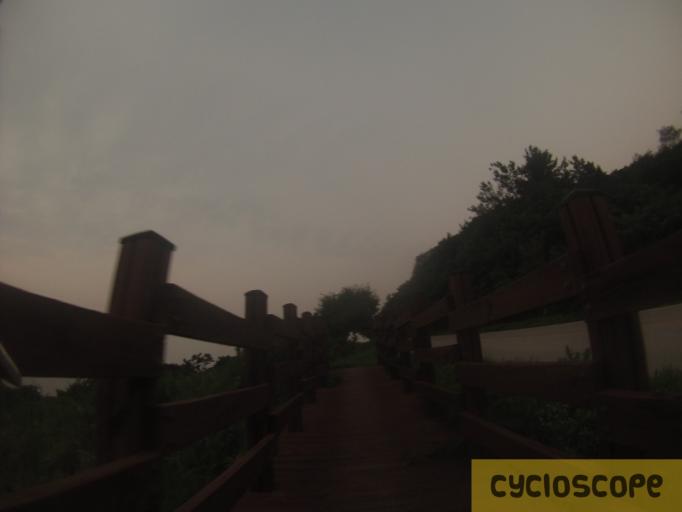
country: KR
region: Jeollabuk-do
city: Puan
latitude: 35.6567
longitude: 126.4977
